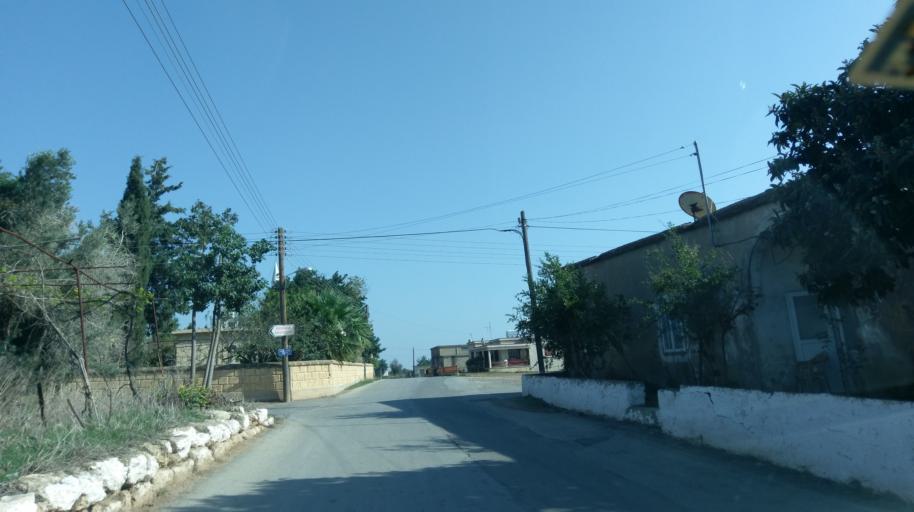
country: CY
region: Ammochostos
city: Leonarisso
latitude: 35.4833
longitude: 34.1880
